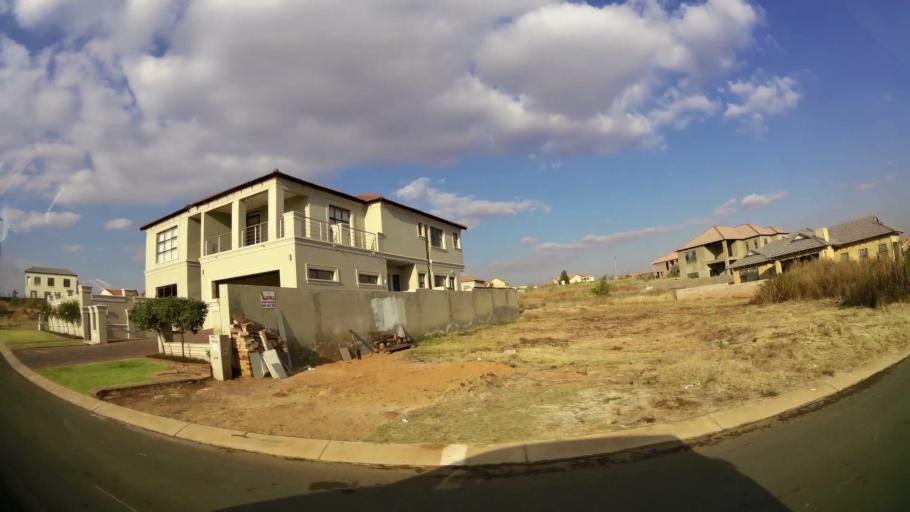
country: ZA
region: Gauteng
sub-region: West Rand District Municipality
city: Krugersdorp
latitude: -26.0999
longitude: 27.7300
